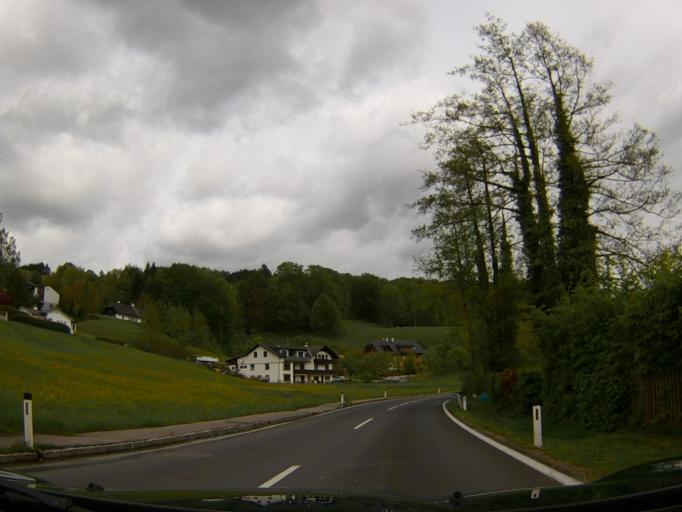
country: AT
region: Upper Austria
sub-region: Politischer Bezirk Vocklabruck
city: Steinbach am Attersee
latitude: 47.8414
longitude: 13.5211
